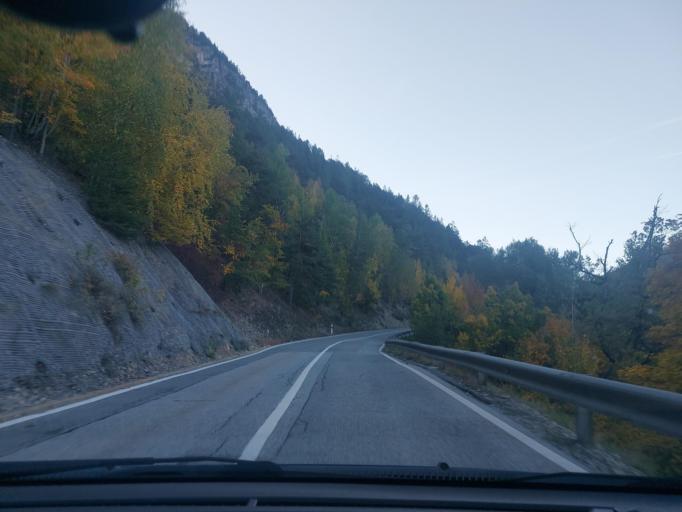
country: CH
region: Valais
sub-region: Sierre District
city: Chippis
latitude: 46.2530
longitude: 7.5745
